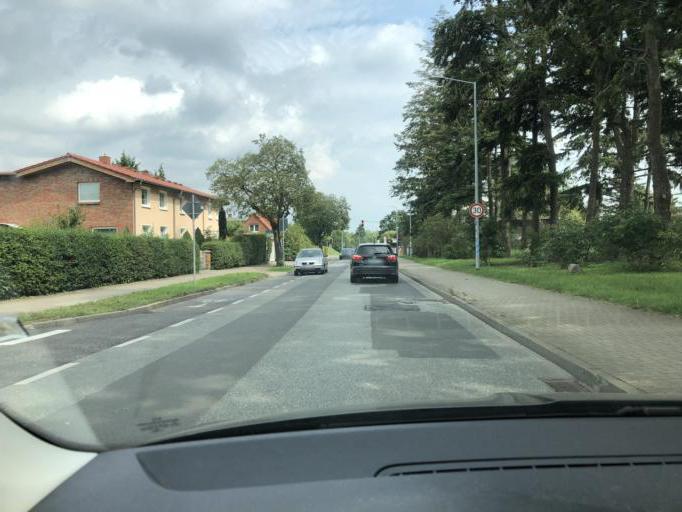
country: DE
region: Mecklenburg-Vorpommern
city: Neumuehle
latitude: 53.6289
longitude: 11.3757
